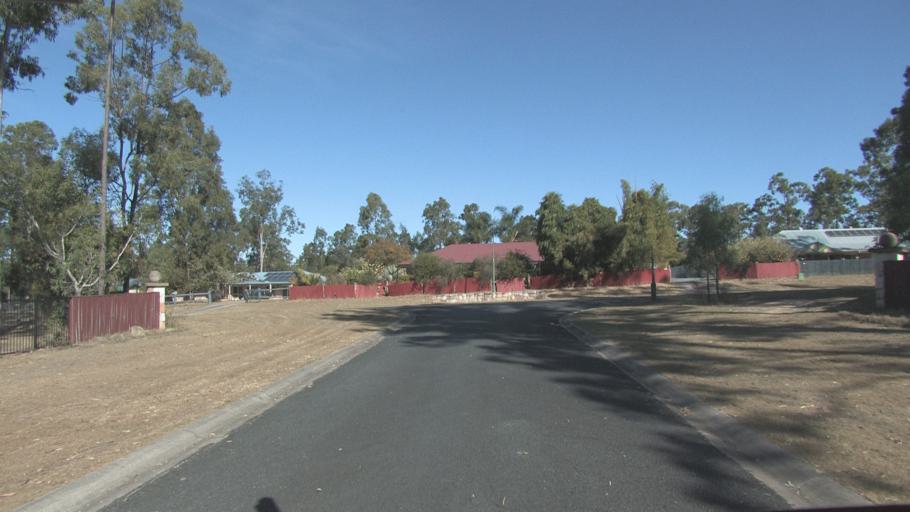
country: AU
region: Queensland
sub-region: Logan
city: North Maclean
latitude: -27.7990
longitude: 152.9744
